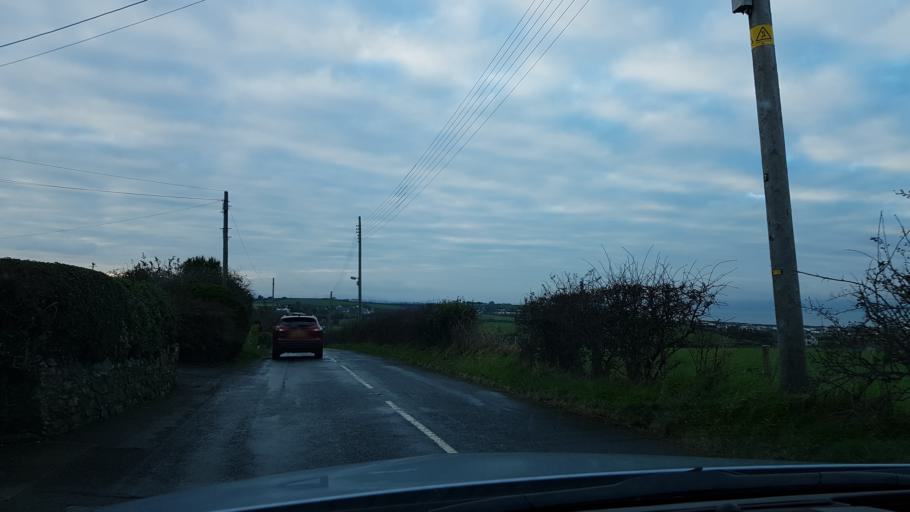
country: GB
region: Northern Ireland
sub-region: Down District
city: Donaghadee
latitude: 54.6724
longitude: -5.5849
